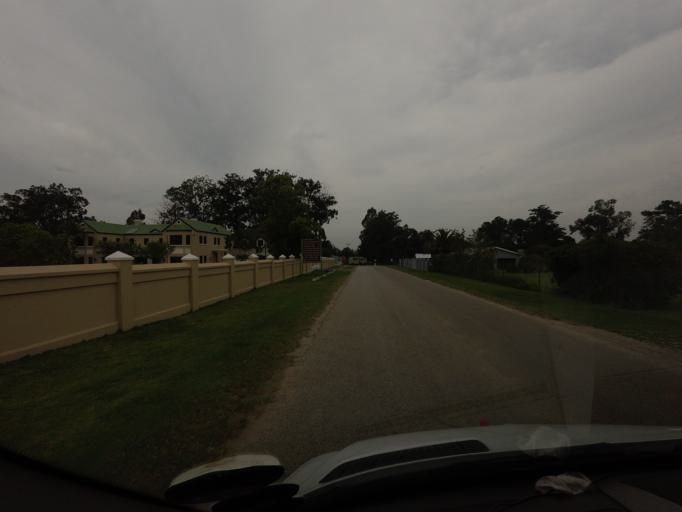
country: ZA
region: Eastern Cape
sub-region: Cacadu District Municipality
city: Kareedouw
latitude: -33.9726
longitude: 23.8864
